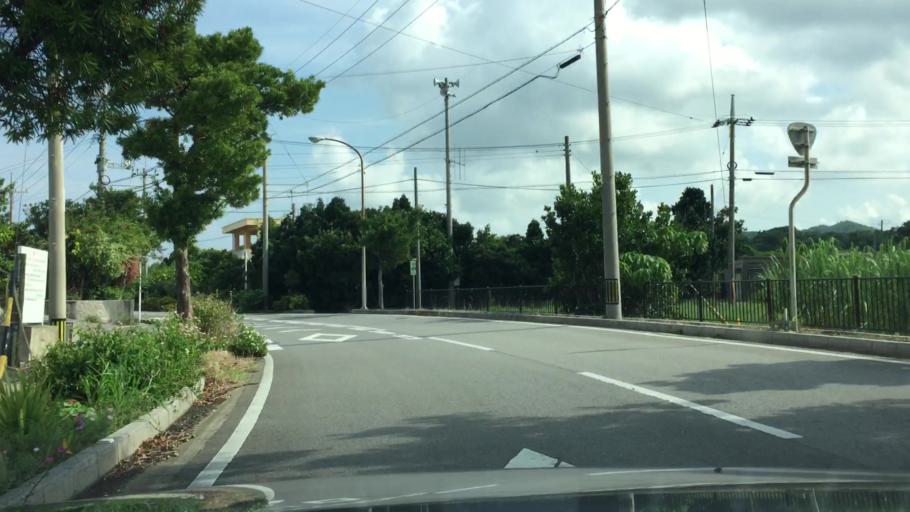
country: JP
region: Okinawa
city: Ishigaki
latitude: 24.4657
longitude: 124.2498
